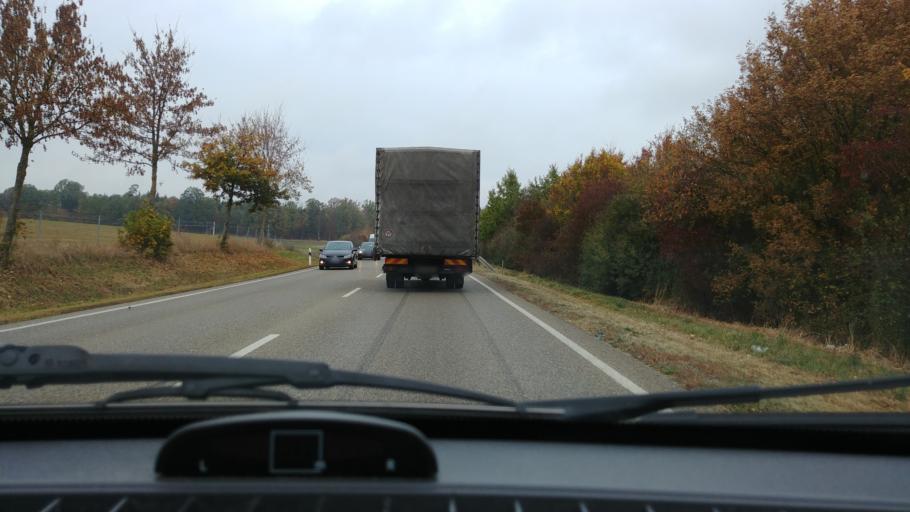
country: DE
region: Baden-Wuerttemberg
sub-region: Regierungsbezirk Stuttgart
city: Aalen
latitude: 48.8482
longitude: 10.0704
